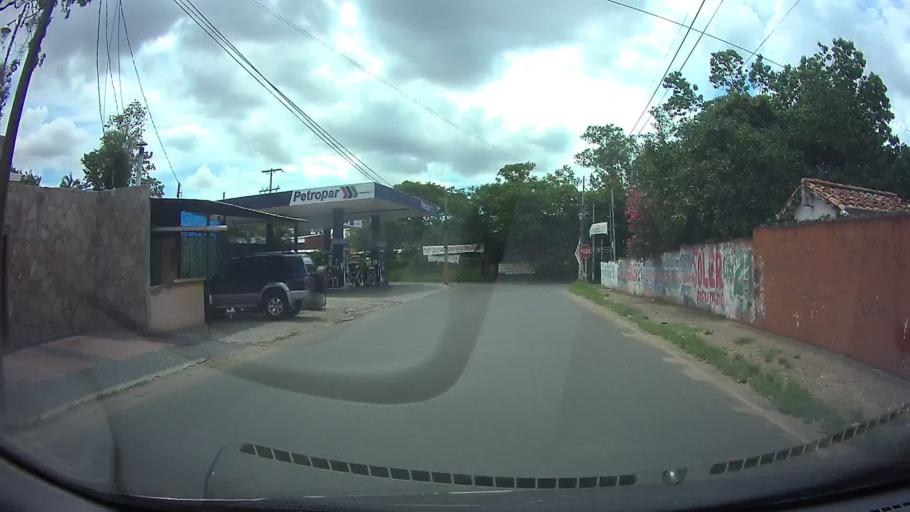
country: PY
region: Central
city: Fernando de la Mora
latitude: -25.3224
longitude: -57.5392
